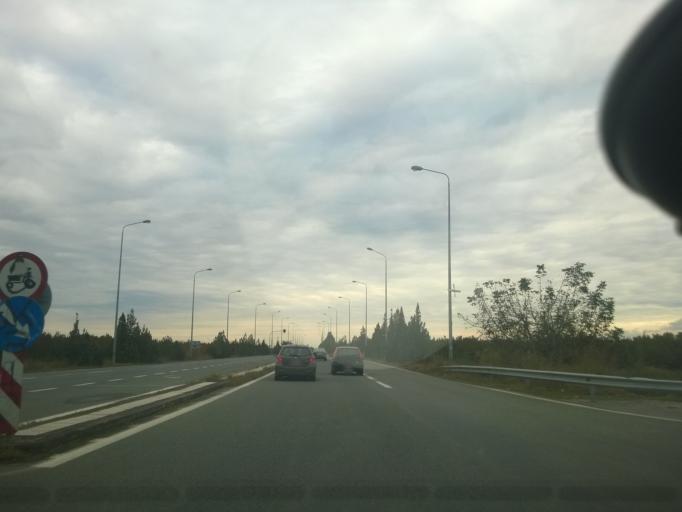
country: GR
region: Central Macedonia
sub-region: Nomos Pellis
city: Palaifyto
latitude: 40.8004
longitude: 22.2616
